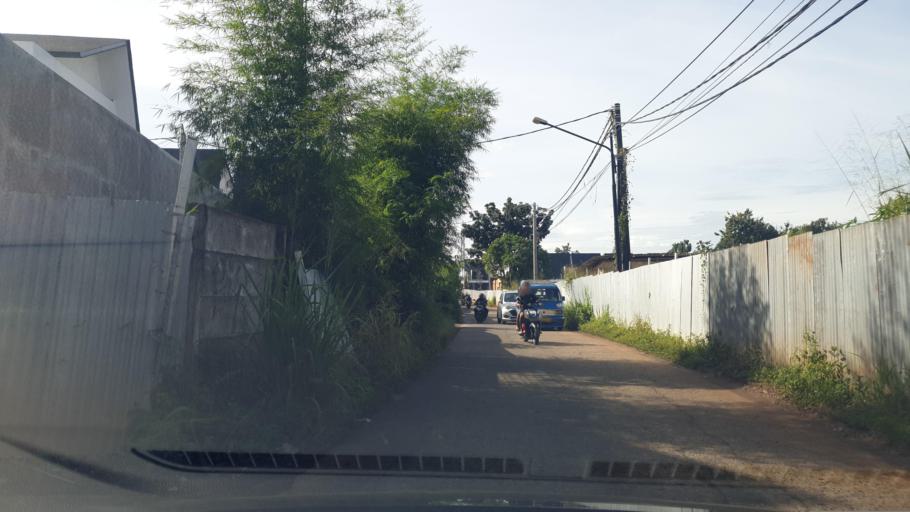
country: ID
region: West Java
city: Sawangan
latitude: -6.3717
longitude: 106.7848
